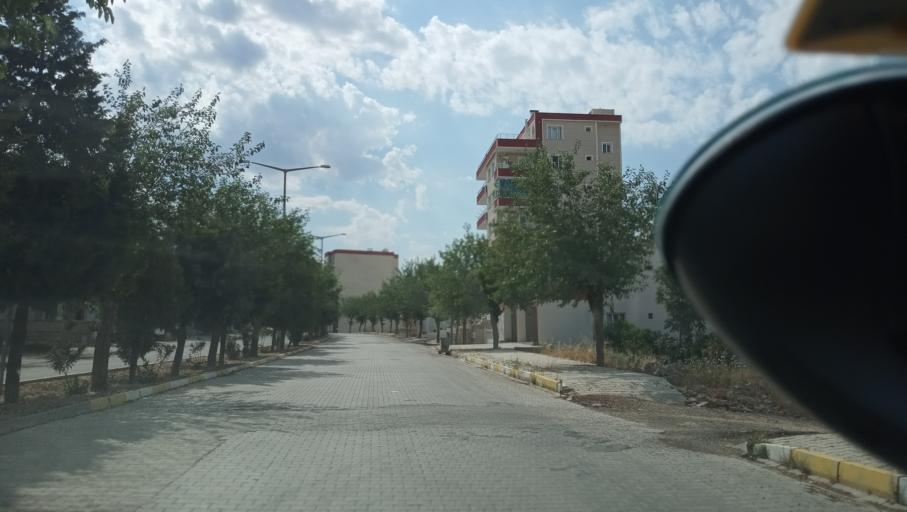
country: TR
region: Mardin
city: Kabala
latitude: 37.3411
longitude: 40.8106
